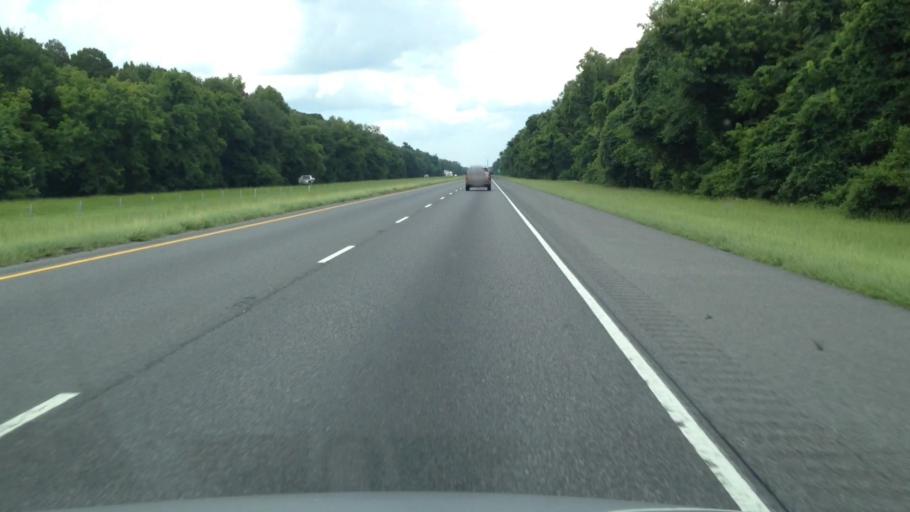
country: US
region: Louisiana
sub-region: Ascension Parish
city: Sorrento
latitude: 30.1641
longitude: -90.8502
